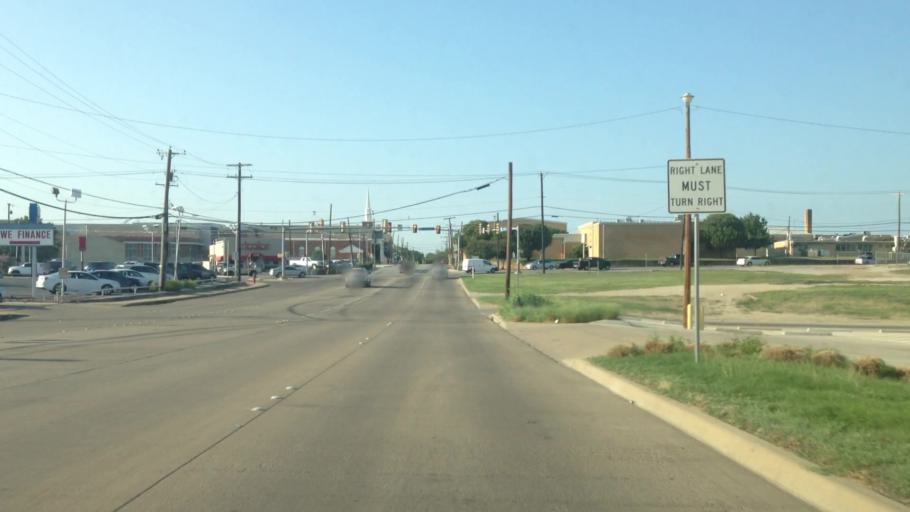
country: US
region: Texas
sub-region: Tarrant County
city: Haltom City
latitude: 32.8037
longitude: -97.2557
